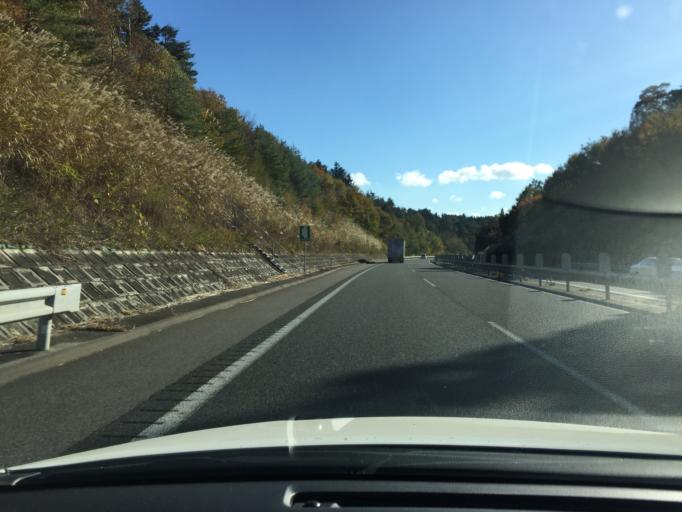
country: JP
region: Fukushima
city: Funehikimachi-funehiki
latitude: 37.3250
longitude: 140.6174
